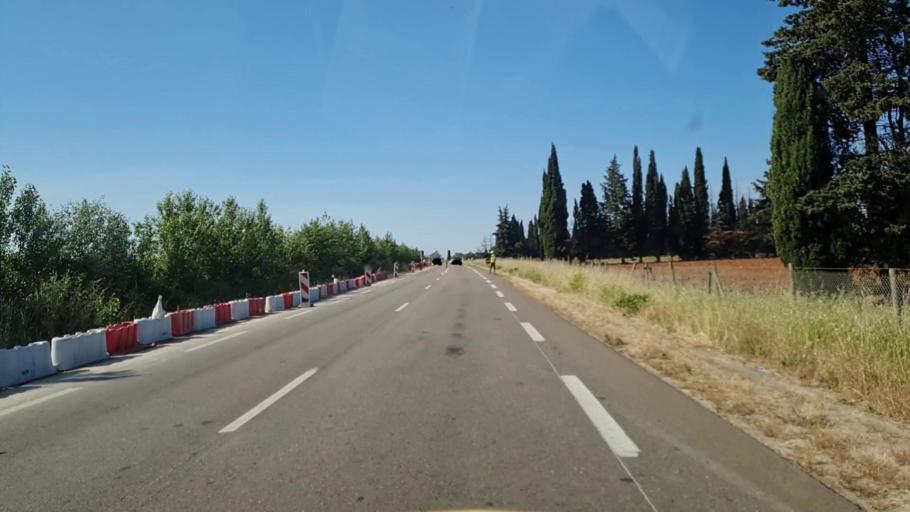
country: FR
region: Languedoc-Roussillon
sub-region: Departement du Gard
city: Garons
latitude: 43.7434
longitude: 4.4089
